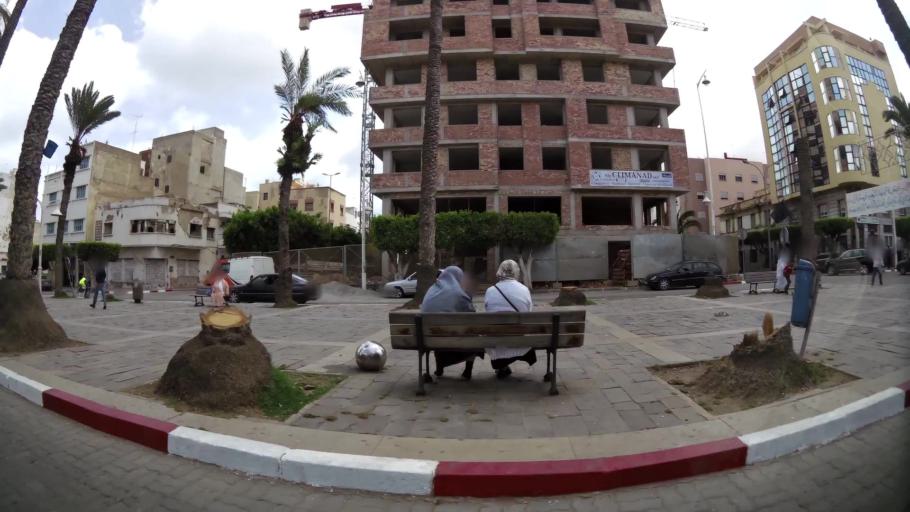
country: MA
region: Oriental
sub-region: Nador
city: Nador
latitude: 35.1798
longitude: -2.9254
